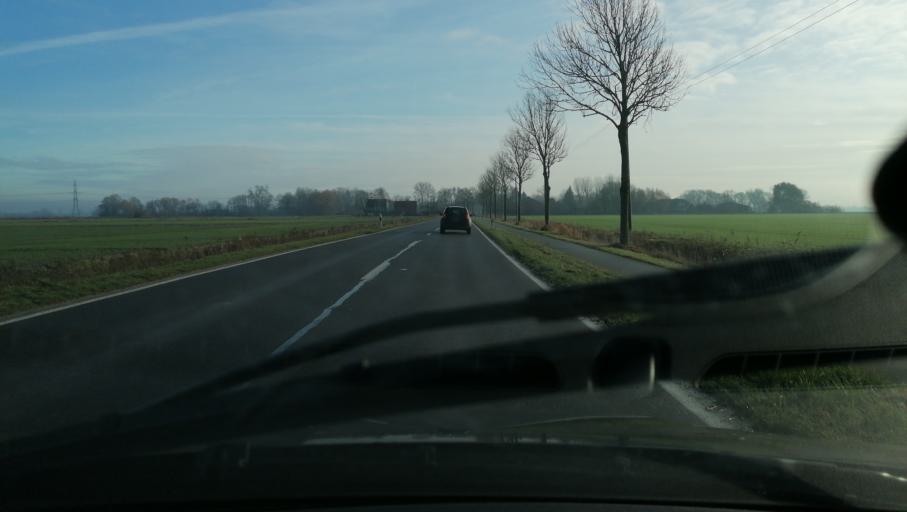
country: DE
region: Schleswig-Holstein
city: Epenwohrden
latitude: 54.1109
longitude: 9.0237
